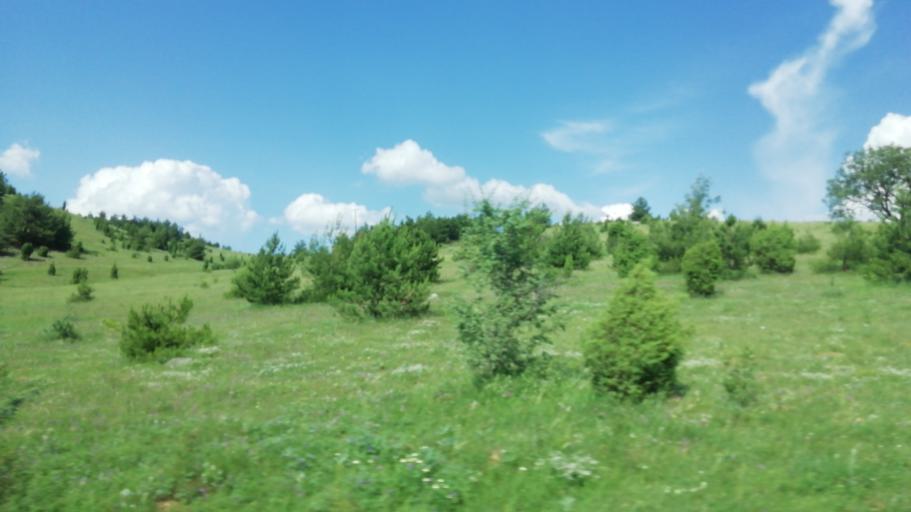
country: TR
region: Karabuk
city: Karabuk
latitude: 41.1305
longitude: 32.5675
